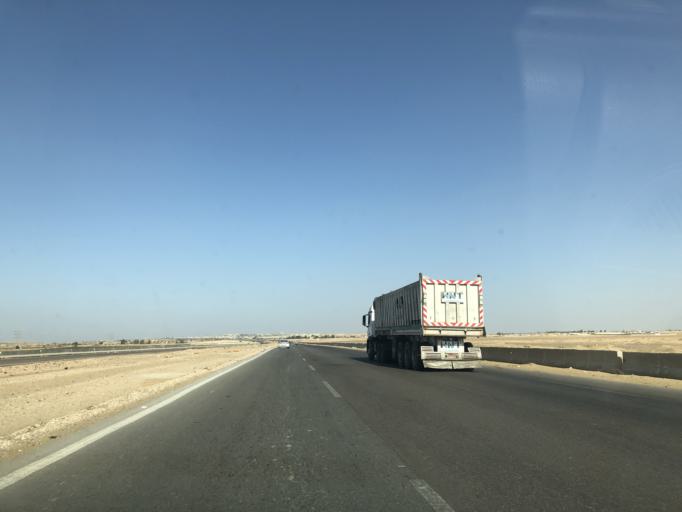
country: EG
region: Muhafazat al Minufiyah
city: Ashmun
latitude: 30.0678
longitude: 30.8913
